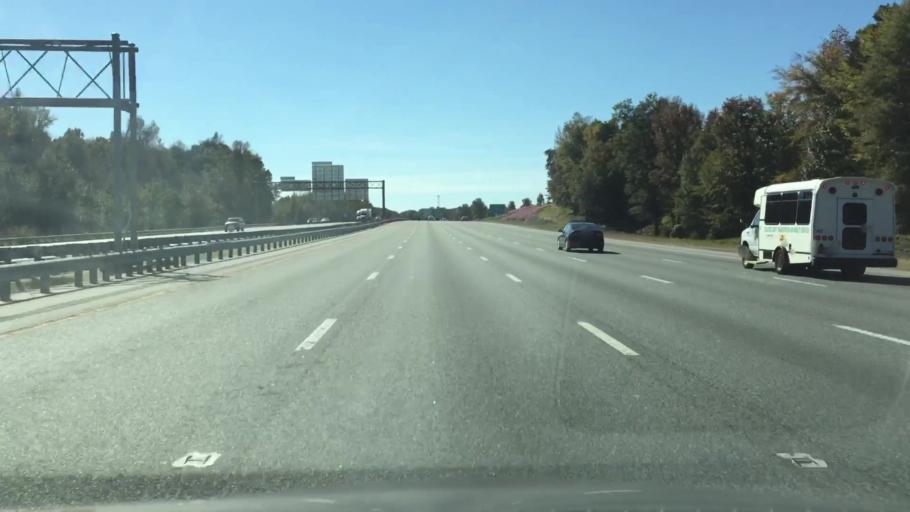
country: US
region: North Carolina
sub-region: Guilford County
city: Jamestown
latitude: 35.9913
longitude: -79.8741
